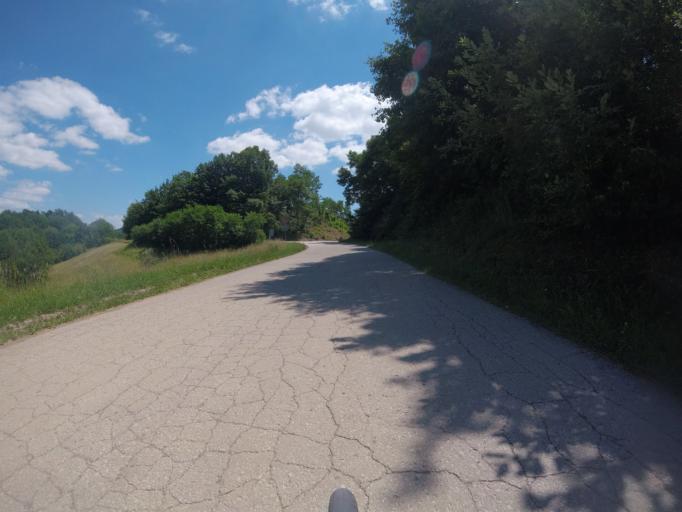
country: HR
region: Karlovacka
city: Ozalj
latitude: 45.6701
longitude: 15.4081
